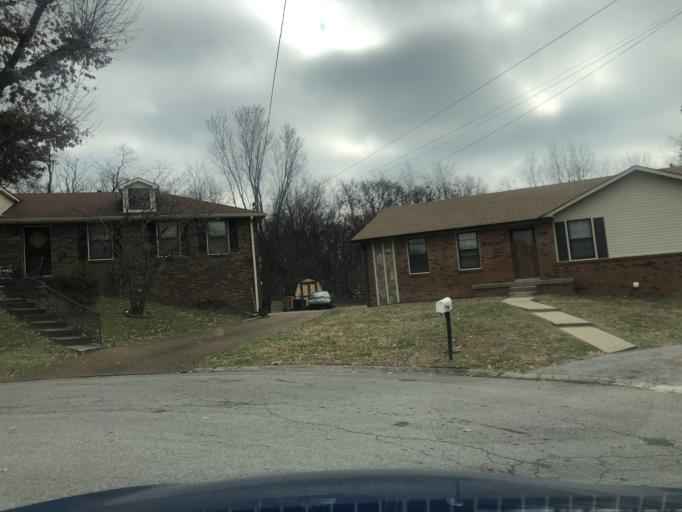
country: US
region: Tennessee
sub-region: Davidson County
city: Oak Hill
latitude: 36.0927
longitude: -86.7115
